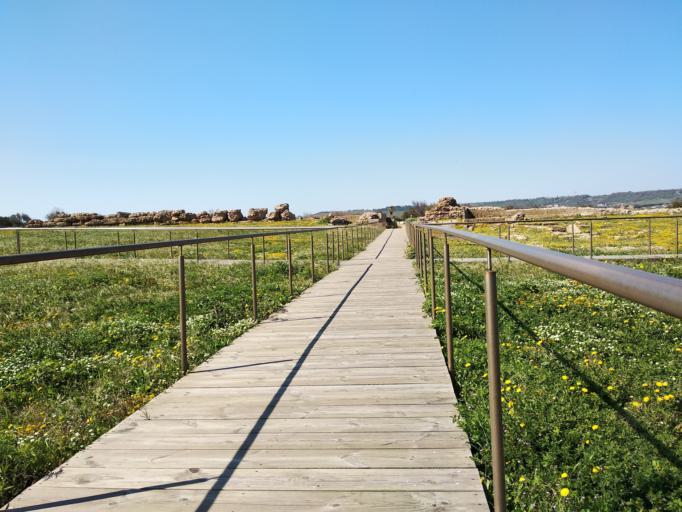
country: IT
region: Calabria
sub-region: Provincia di Crotone
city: Crotone
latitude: 39.0267
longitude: 17.2043
